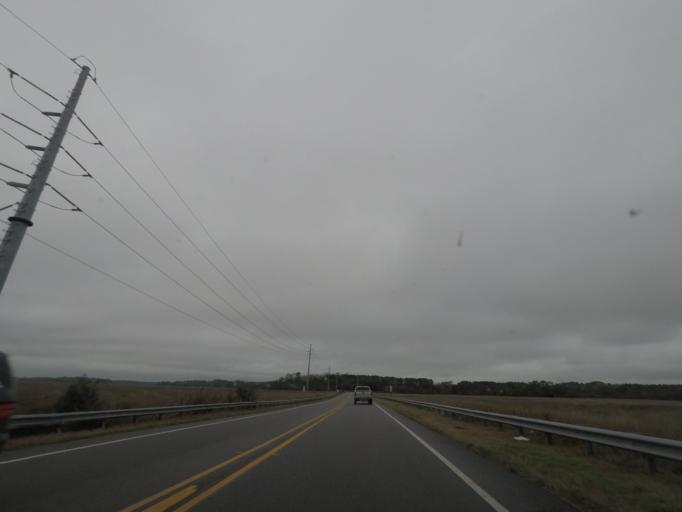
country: US
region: South Carolina
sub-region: Charleston County
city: Meggett
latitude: 32.6473
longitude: -80.3432
